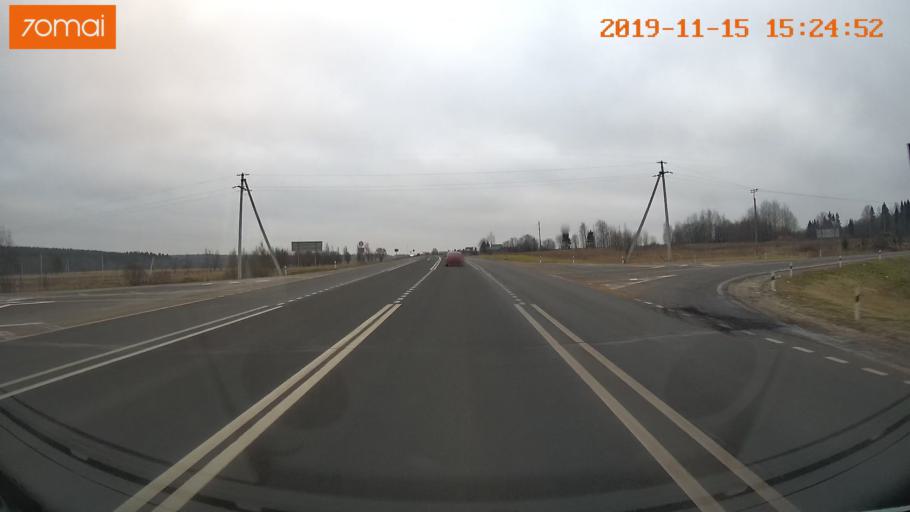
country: RU
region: Jaroslavl
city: Danilov
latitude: 58.1718
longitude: 40.1340
